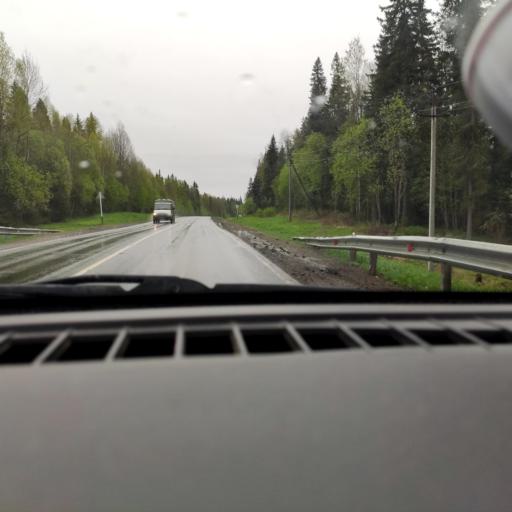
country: RU
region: Perm
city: Perm
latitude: 58.2028
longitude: 56.2026
